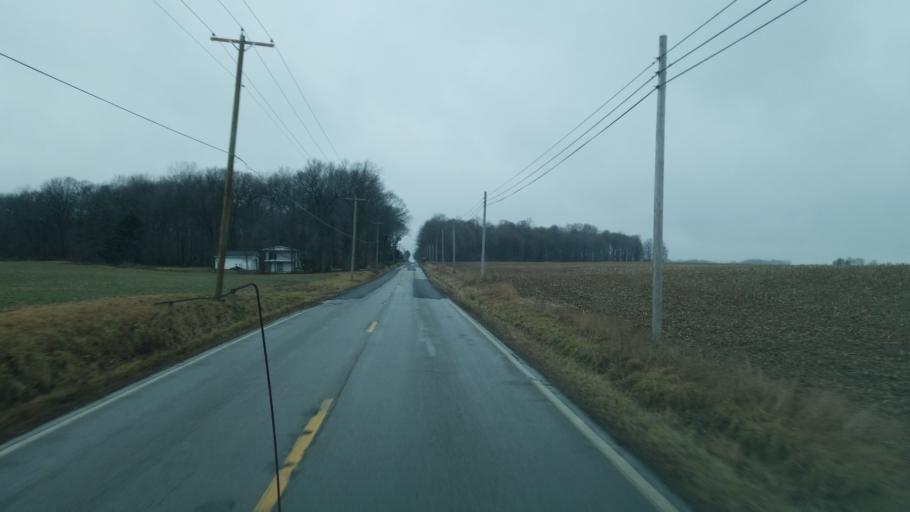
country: US
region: Ohio
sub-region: Wayne County
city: Orrville
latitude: 40.8591
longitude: -81.7970
